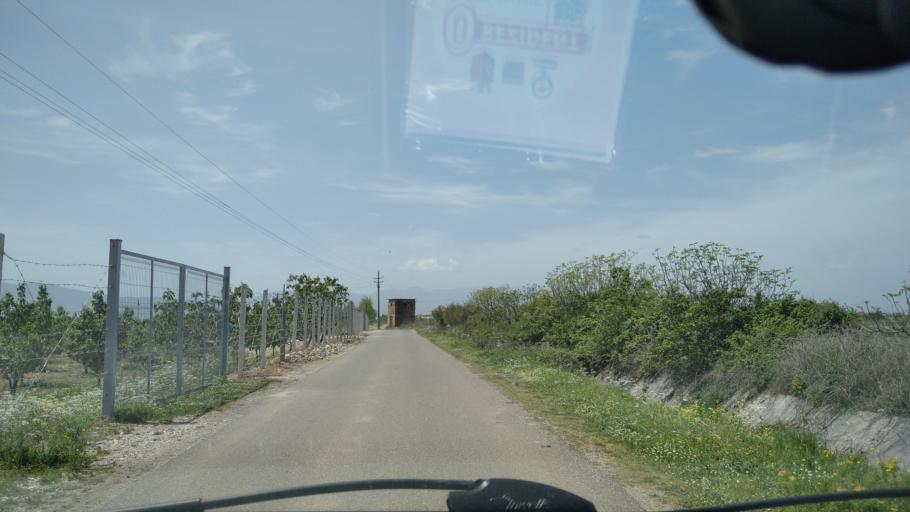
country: AL
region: Shkoder
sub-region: Rrethi i Malesia e Madhe
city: Gruemire
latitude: 42.1462
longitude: 19.5308
